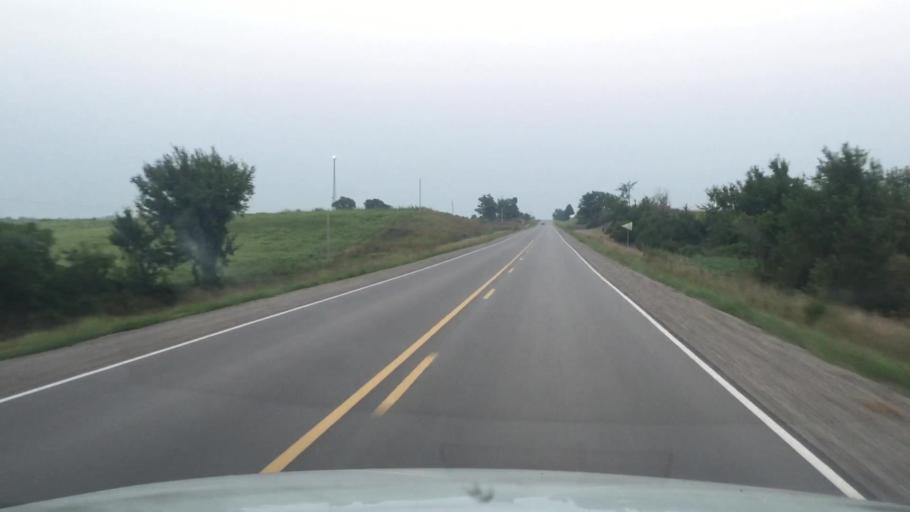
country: US
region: Iowa
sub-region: Marion County
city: Melcher-Dallas
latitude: 41.1895
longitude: -93.4143
